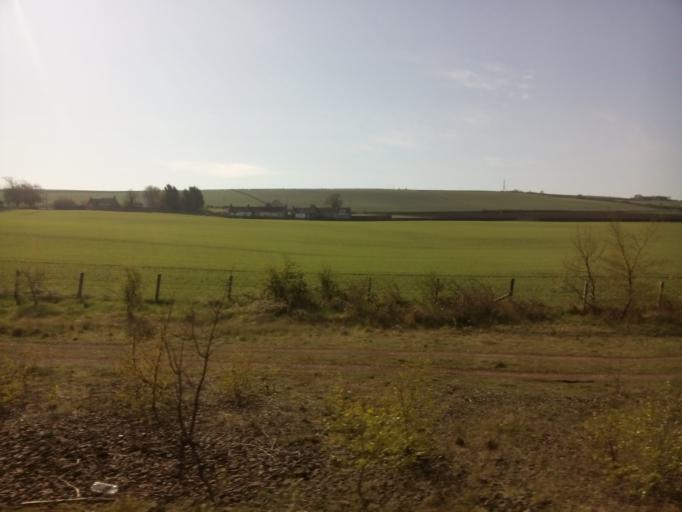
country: GB
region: Scotland
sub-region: East Lothian
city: Prestonpans
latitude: 55.9469
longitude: -2.9935
